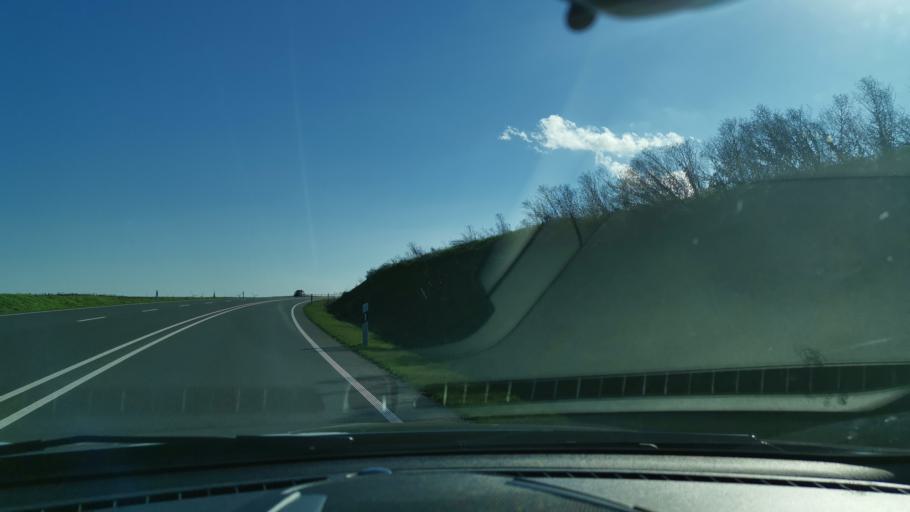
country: DE
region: North Rhine-Westphalia
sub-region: Regierungsbezirk Dusseldorf
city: Rommerskirchen
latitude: 51.0471
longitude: 6.6656
